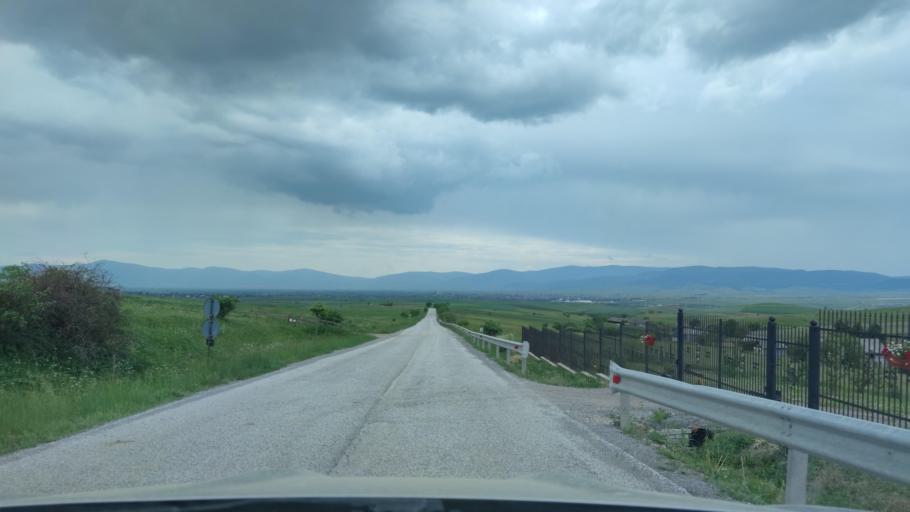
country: RO
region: Harghita
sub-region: Comuna Ditrau
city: Ditrau
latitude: 46.8454
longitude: 25.5011
